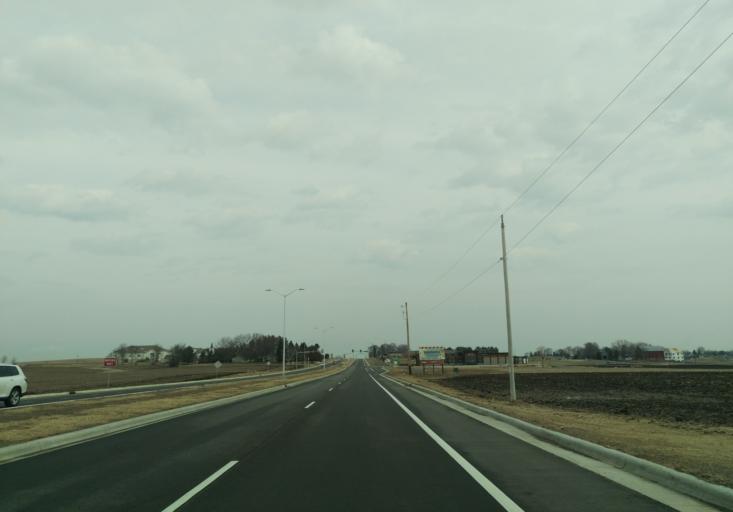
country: US
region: Wisconsin
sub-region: Dane County
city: Waunakee
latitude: 43.1667
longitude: -89.4618
